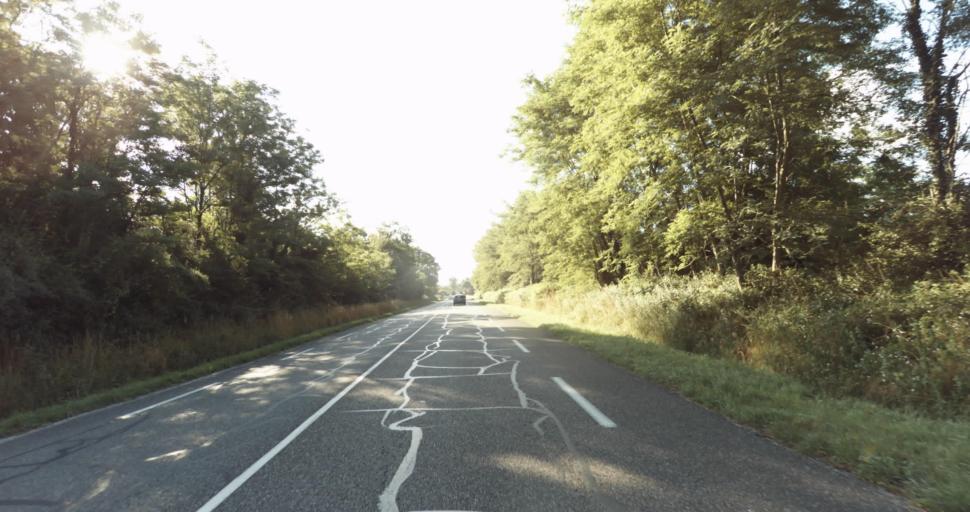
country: FR
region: Aquitaine
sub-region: Departement de la Gironde
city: Bazas
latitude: 44.4563
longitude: -0.2542
